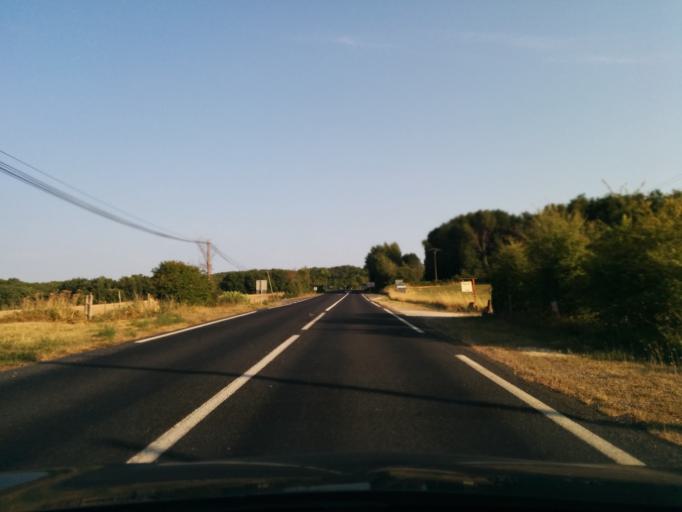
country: FR
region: Midi-Pyrenees
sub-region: Departement du Lot
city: Le Vigan
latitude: 44.7747
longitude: 1.4755
